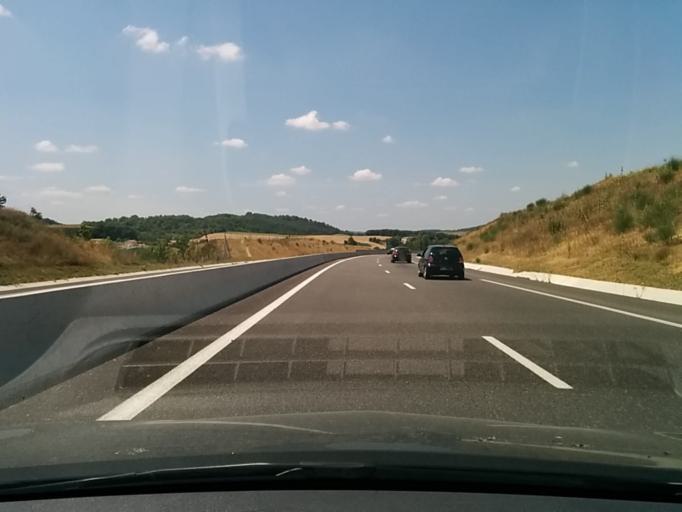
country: FR
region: Midi-Pyrenees
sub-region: Departement du Gers
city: Preignan
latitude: 43.6518
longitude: 0.6733
